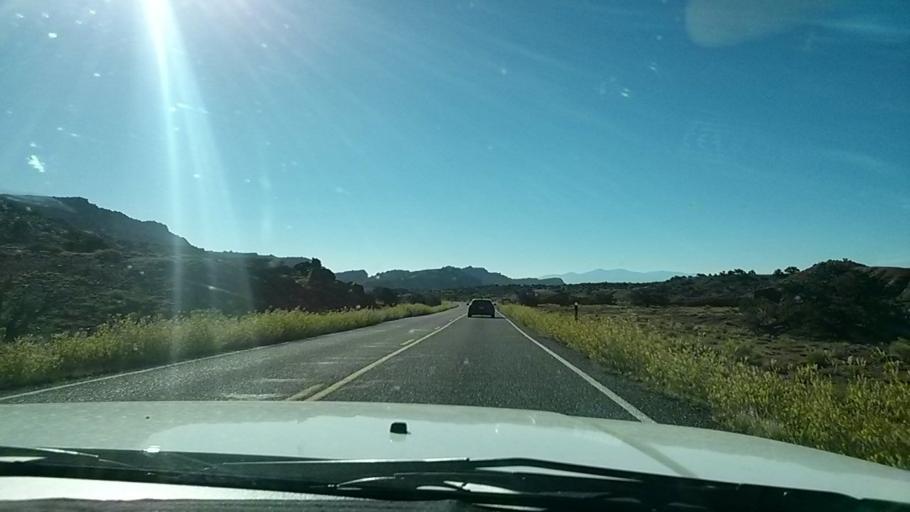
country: US
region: Utah
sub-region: Wayne County
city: Loa
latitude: 38.3237
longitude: -111.3474
